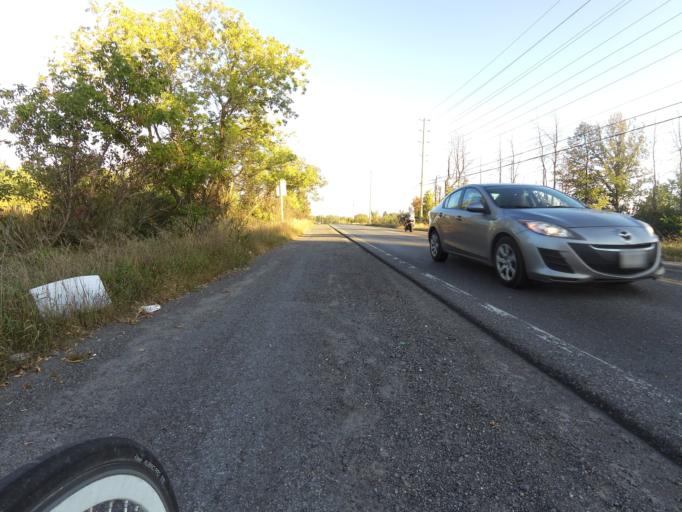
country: CA
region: Ontario
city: Bells Corners
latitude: 45.2650
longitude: -75.7403
